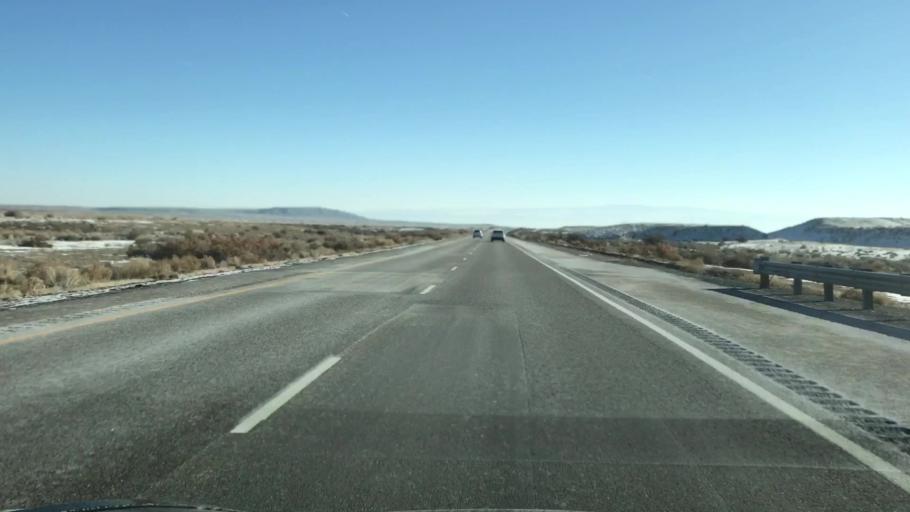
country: US
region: Utah
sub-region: Grand County
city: Moab
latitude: 38.9403
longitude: -109.5233
